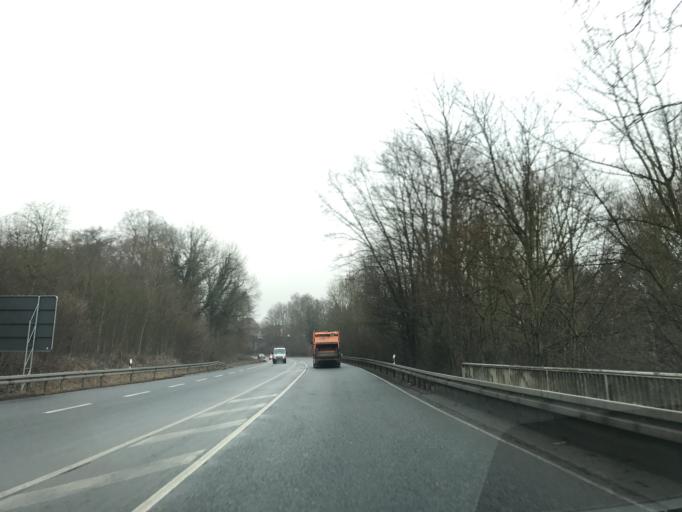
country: DE
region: Hesse
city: Grebenstein
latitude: 51.4437
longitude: 9.4104
